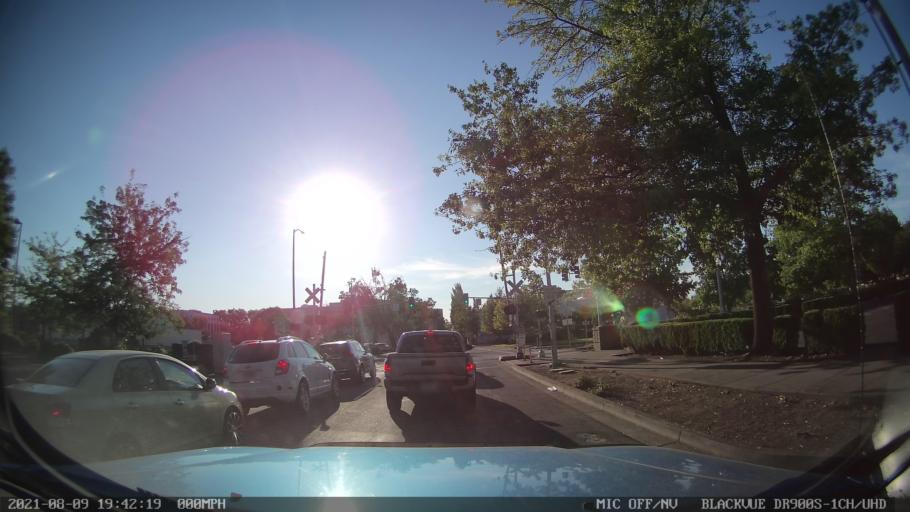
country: US
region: Oregon
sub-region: Marion County
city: Salem
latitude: 44.9412
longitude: -123.0248
